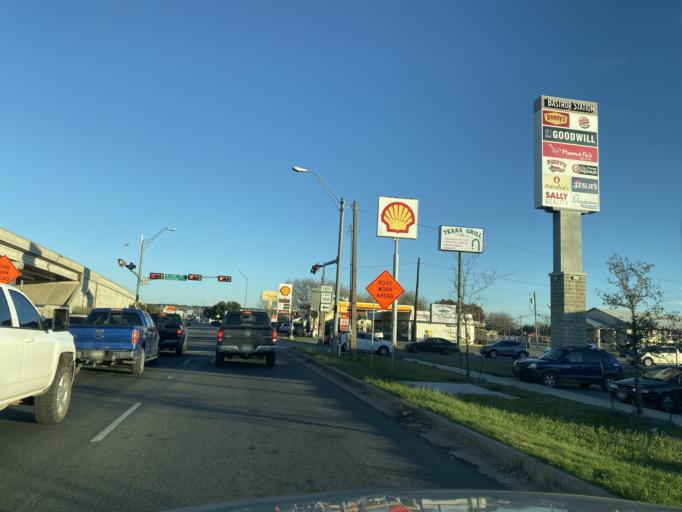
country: US
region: Texas
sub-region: Bastrop County
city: Bastrop
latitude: 30.1050
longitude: -97.3297
